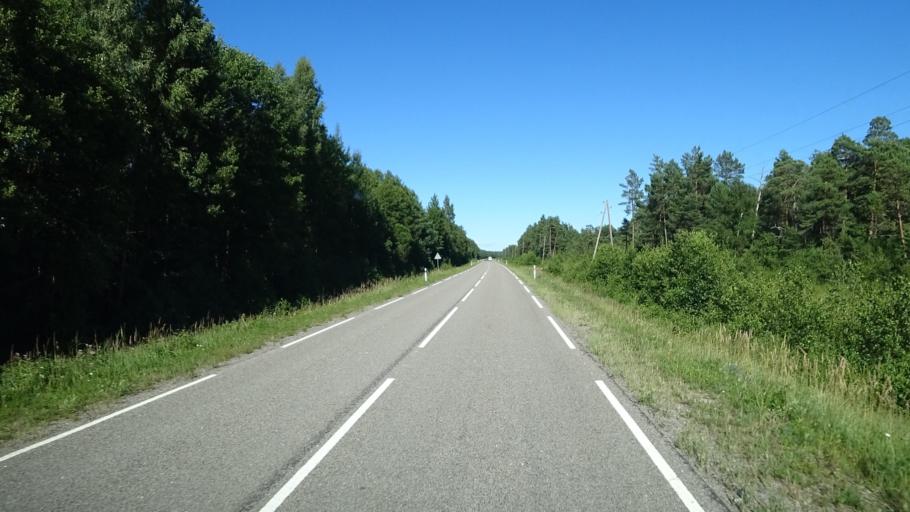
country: LV
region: Dundaga
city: Dundaga
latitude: 57.7105
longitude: 22.4472
